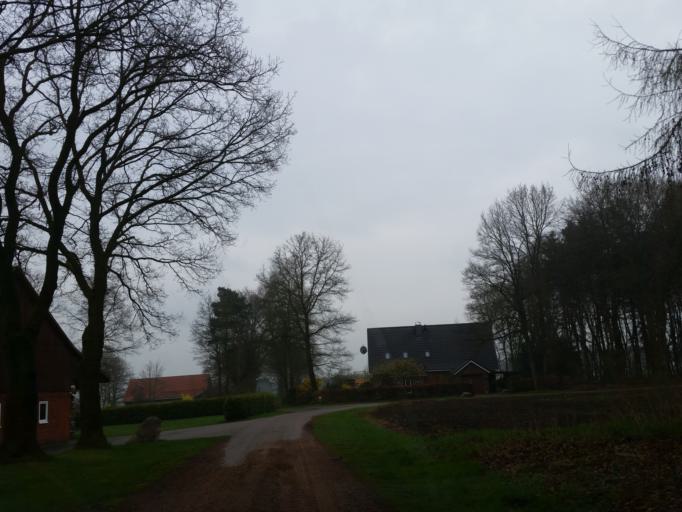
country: DE
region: Lower Saxony
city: Hipstedt
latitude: 53.5676
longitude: 8.9787
